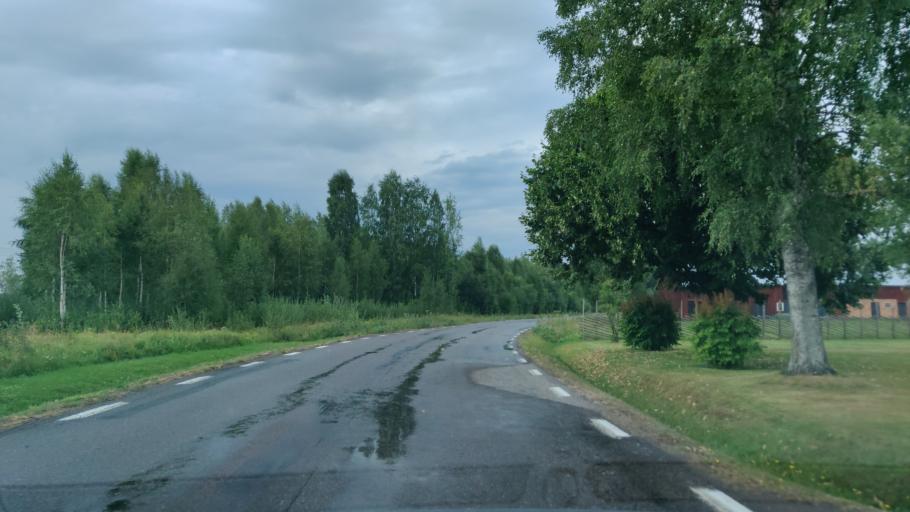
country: SE
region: Vaermland
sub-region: Munkfors Kommun
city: Munkfors
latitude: 59.8808
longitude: 13.5216
